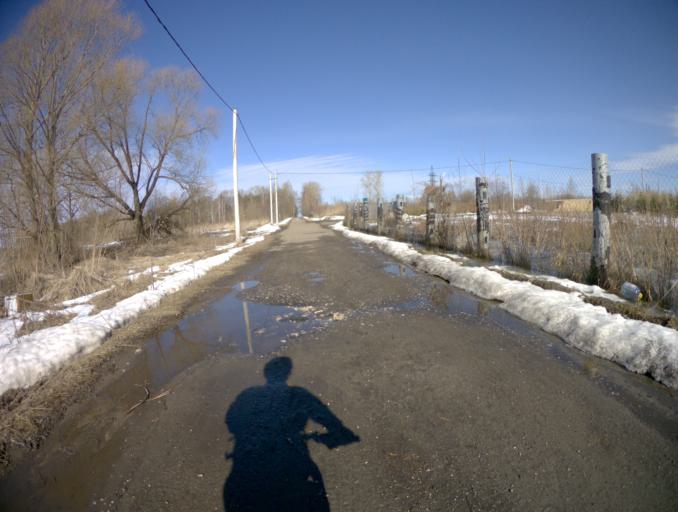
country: RU
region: Vladimir
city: Suzdal'
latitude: 56.4277
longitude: 40.4585
